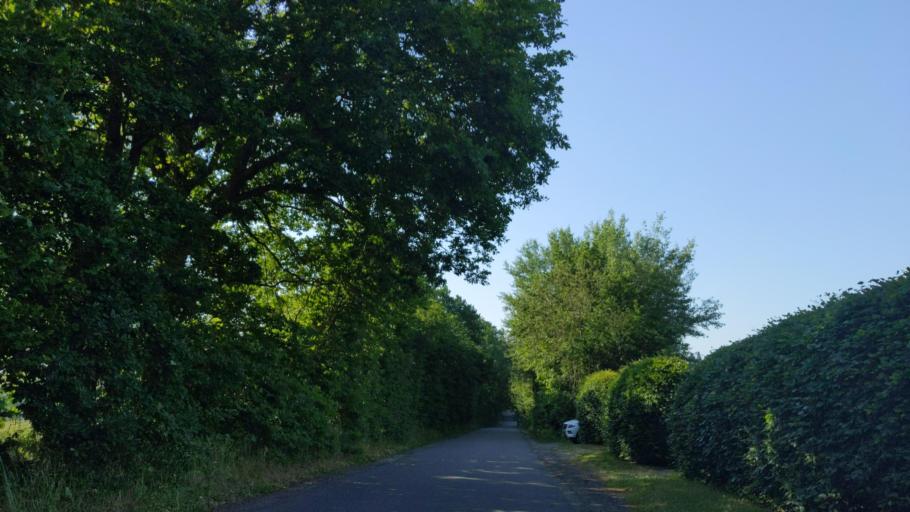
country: DE
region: Schleswig-Holstein
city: Ratekau
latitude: 53.9280
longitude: 10.7670
